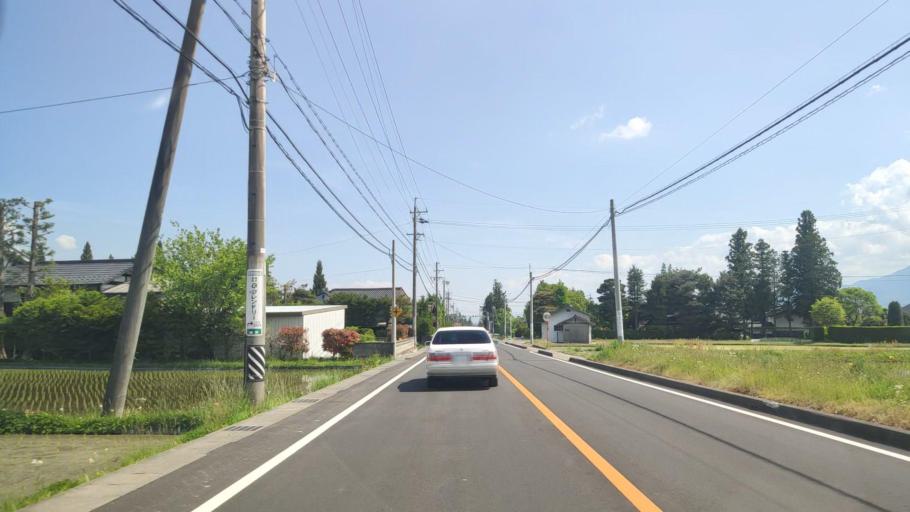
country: JP
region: Nagano
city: Hotaka
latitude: 36.3991
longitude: 137.8618
